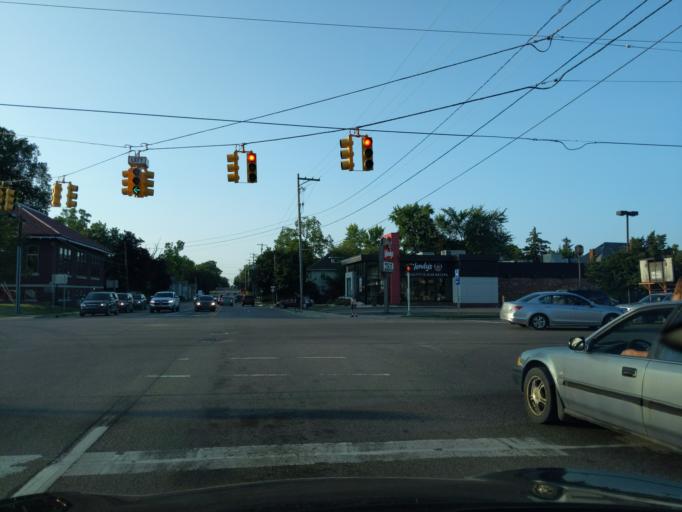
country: US
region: Michigan
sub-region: Shiawassee County
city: Owosso
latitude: 42.9974
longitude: -84.1768
